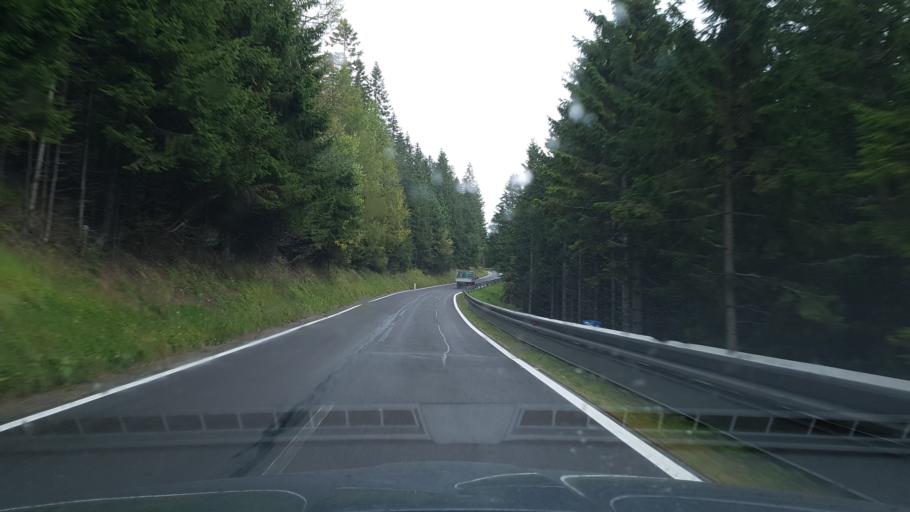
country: AT
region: Styria
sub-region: Politischer Bezirk Voitsberg
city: Salla
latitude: 47.1107
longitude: 14.9093
